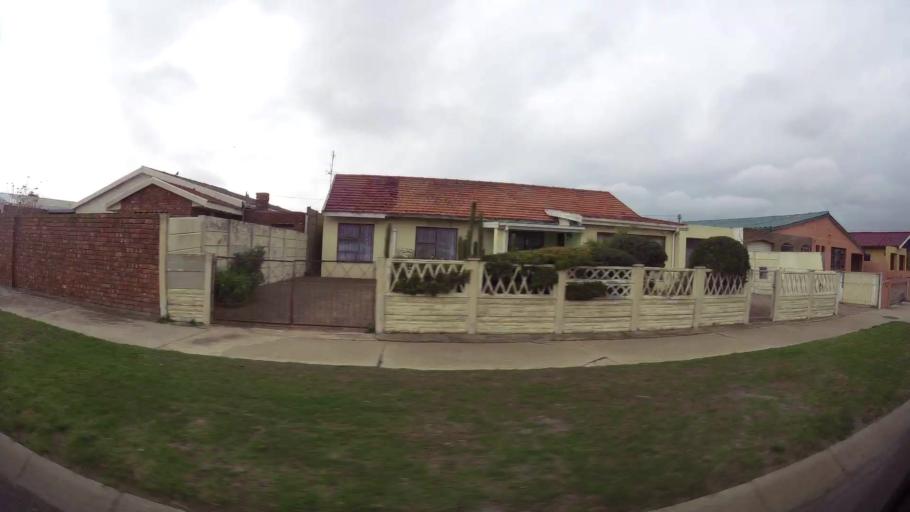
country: ZA
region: Eastern Cape
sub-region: Nelson Mandela Bay Metropolitan Municipality
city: Port Elizabeth
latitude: -33.9003
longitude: 25.5524
